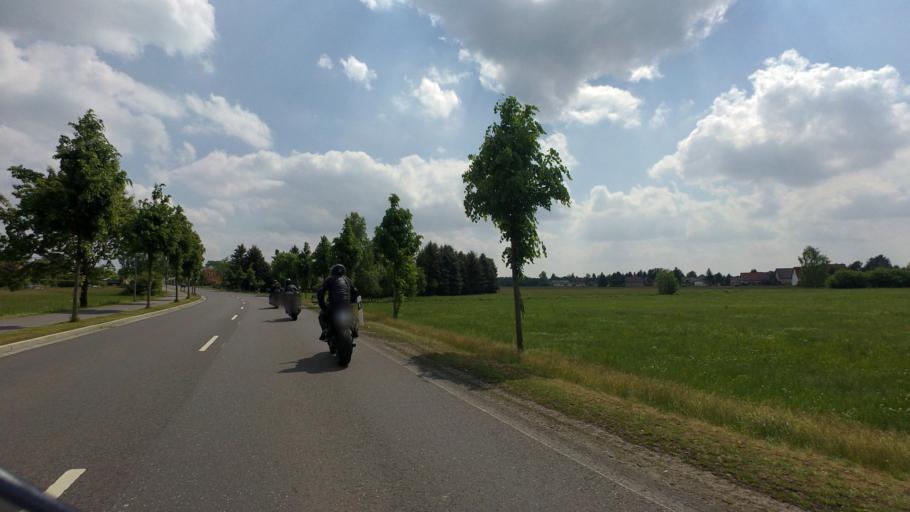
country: DE
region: Saxony
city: Weisskeissel
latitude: 51.4967
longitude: 14.7165
